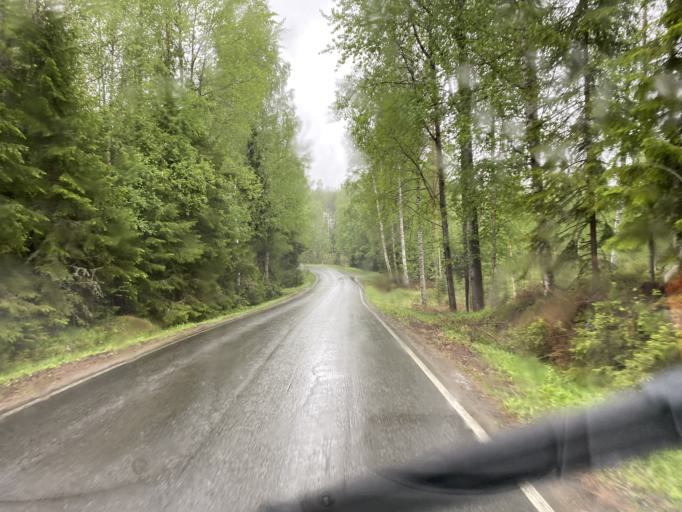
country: FI
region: Haeme
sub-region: Forssa
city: Humppila
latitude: 61.0903
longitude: 23.3109
